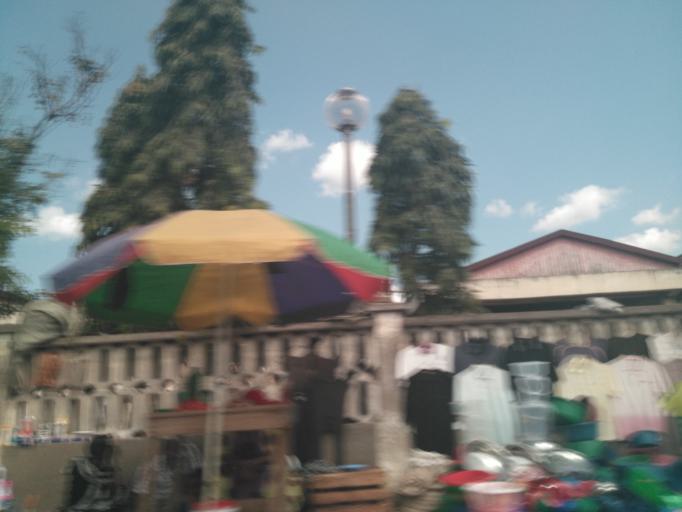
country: TZ
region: Dar es Salaam
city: Dar es Salaam
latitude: -6.8192
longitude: 39.2996
